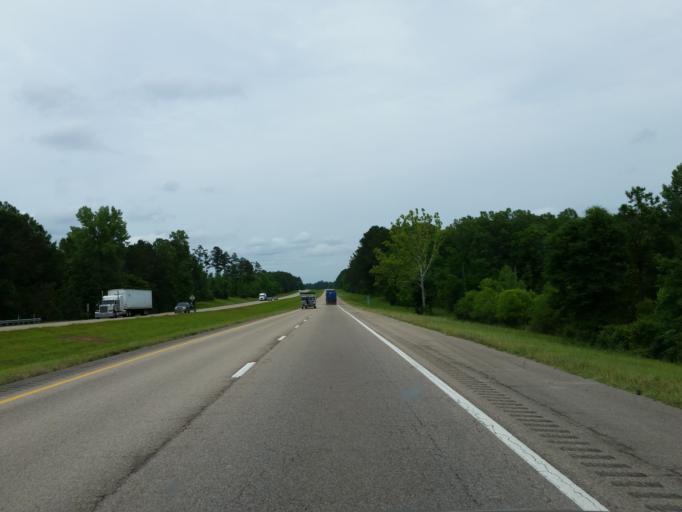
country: US
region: Mississippi
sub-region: Clarke County
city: Stonewall
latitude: 32.0007
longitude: -88.9372
